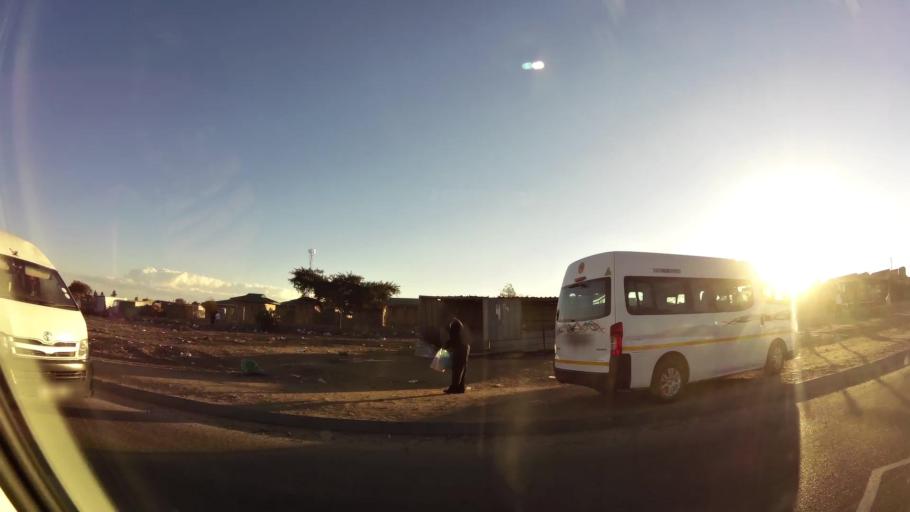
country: ZA
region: Limpopo
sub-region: Capricorn District Municipality
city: Polokwane
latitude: -23.8473
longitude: 29.3541
